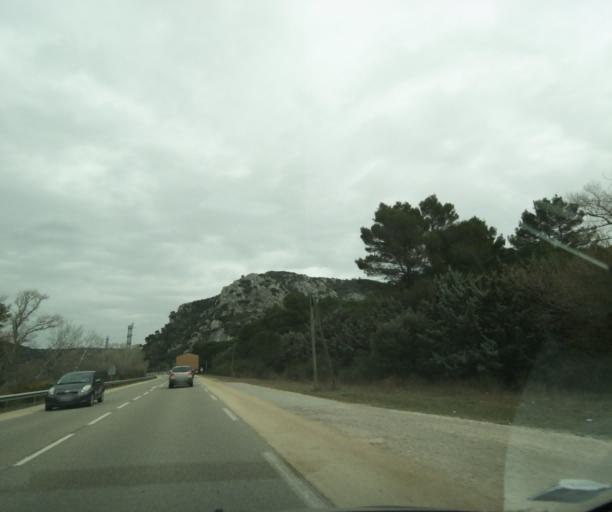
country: FR
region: Provence-Alpes-Cote d'Azur
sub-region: Departement des Bouches-du-Rhone
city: Jouques
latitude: 43.6782
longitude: 5.6541
